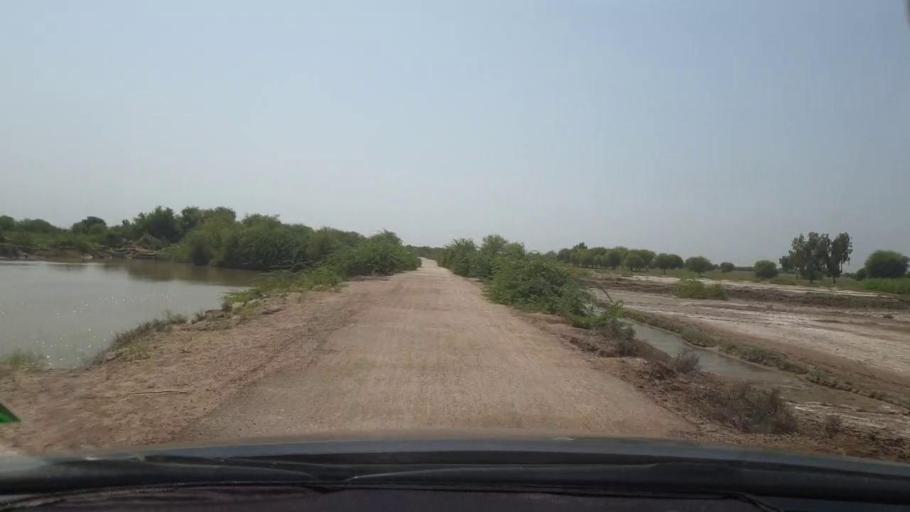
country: PK
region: Sindh
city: Tando Bago
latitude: 24.7916
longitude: 69.1783
